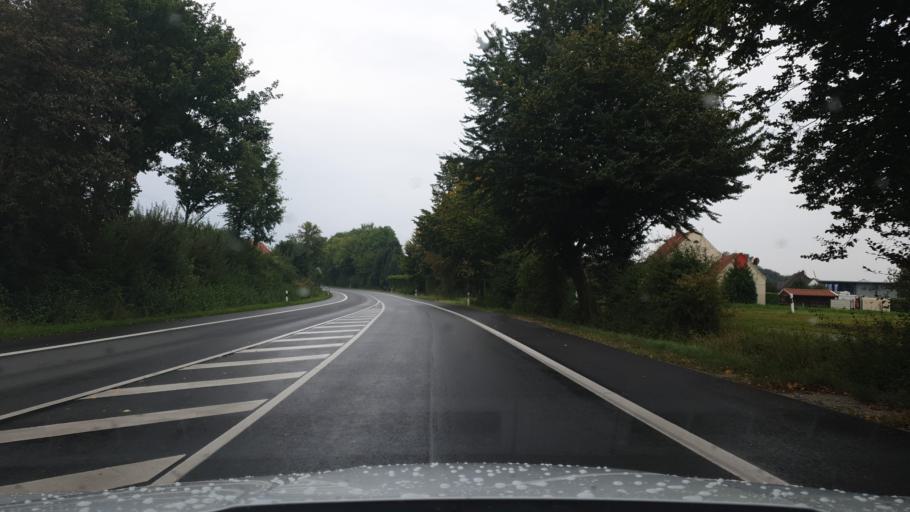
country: DE
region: North Rhine-Westphalia
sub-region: Regierungsbezirk Detmold
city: Kirchlengern
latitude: 52.2308
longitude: 8.6343
